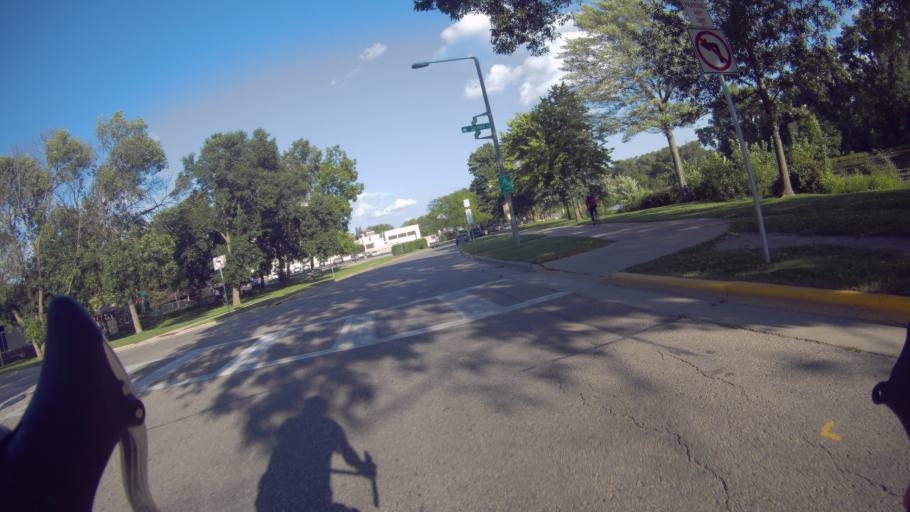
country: US
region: Wisconsin
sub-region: Dane County
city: Madison
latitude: 43.0583
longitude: -89.4071
